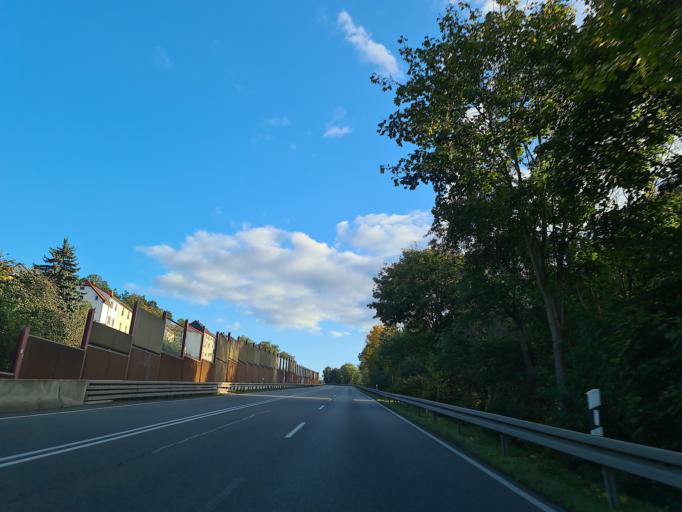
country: DE
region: Thuringia
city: Weida
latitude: 50.7766
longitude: 12.0674
